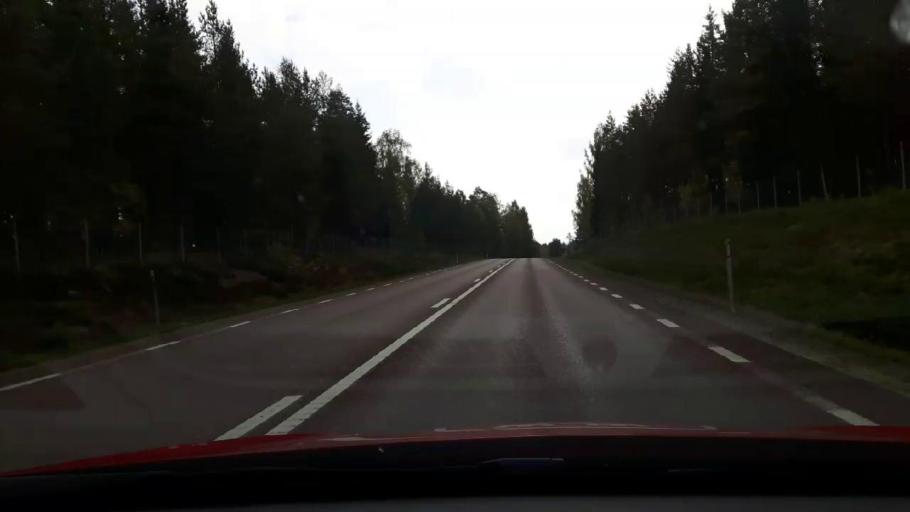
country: SE
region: Gaevleborg
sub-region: Bollnas Kommun
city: Kilafors
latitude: 61.2649
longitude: 16.5483
